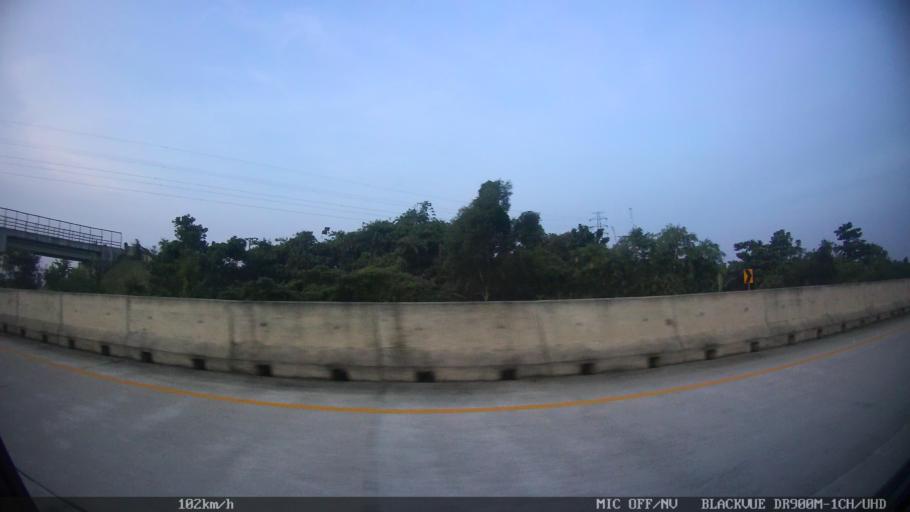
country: ID
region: Lampung
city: Pasuruan
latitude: -5.7199
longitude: 105.6624
